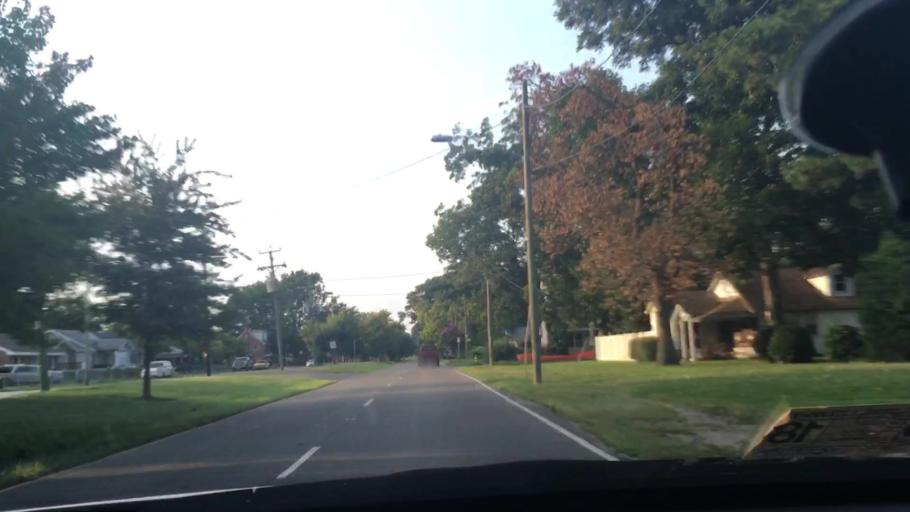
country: US
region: Virginia
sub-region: City of Norfolk
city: Norfolk
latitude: 36.9373
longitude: -76.2448
